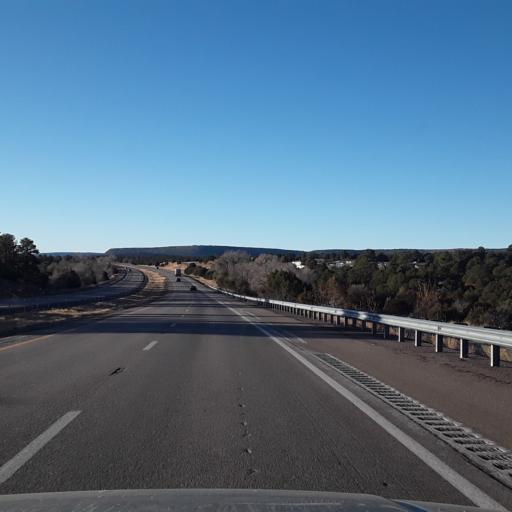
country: US
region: New Mexico
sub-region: San Miguel County
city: Las Vegas
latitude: 35.4923
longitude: -105.2693
